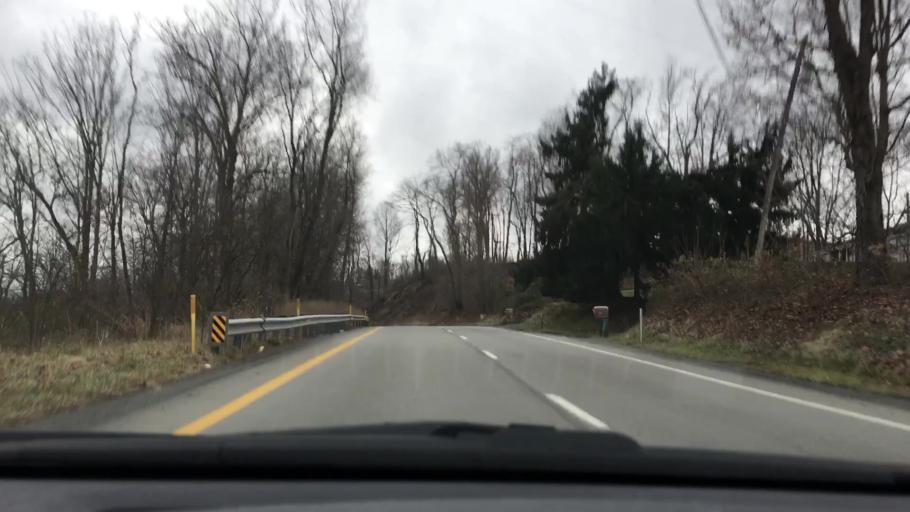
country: US
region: Pennsylvania
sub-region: Fayette County
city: Oliver
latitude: 39.9455
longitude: -79.7338
